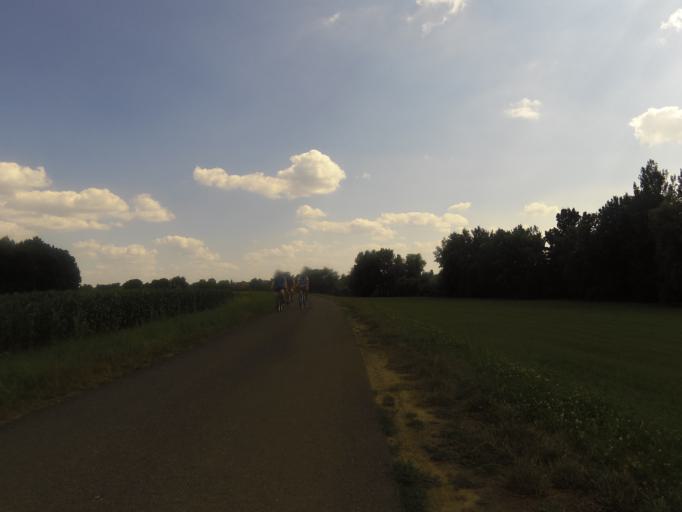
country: HU
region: Jasz-Nagykun-Szolnok
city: Tiszafured
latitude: 47.6166
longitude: 20.7256
